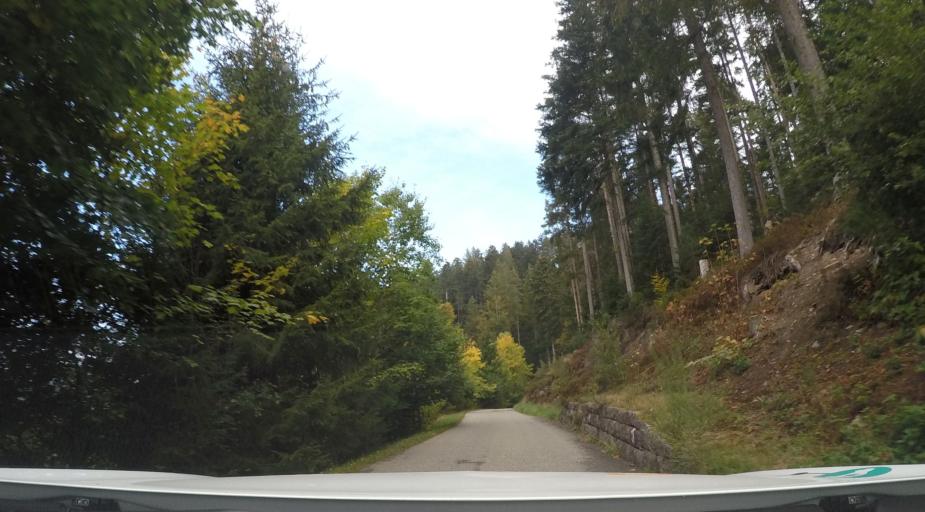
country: DE
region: Baden-Wuerttemberg
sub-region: Karlsruhe Region
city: Baiersbronn
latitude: 48.5453
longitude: 8.3530
